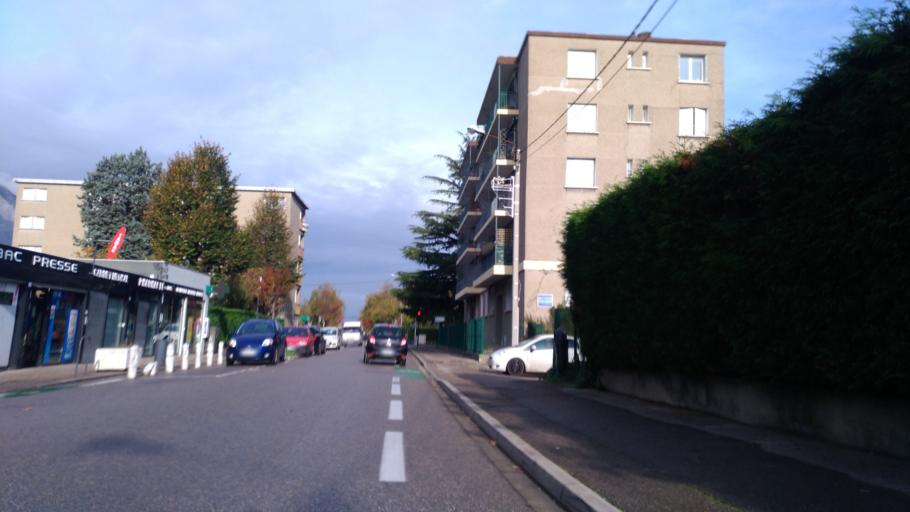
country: FR
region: Rhone-Alpes
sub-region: Departement de l'Isere
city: Fontaine
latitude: 45.1972
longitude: 5.6813
